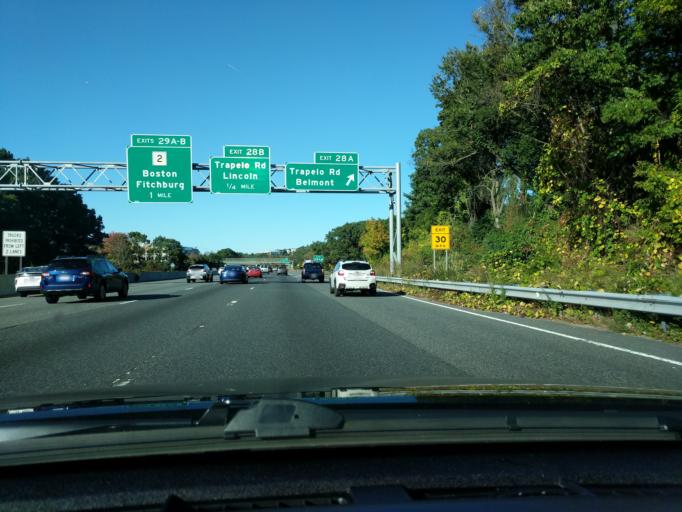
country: US
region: Massachusetts
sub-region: Middlesex County
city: Waltham
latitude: 42.4119
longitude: -71.2577
